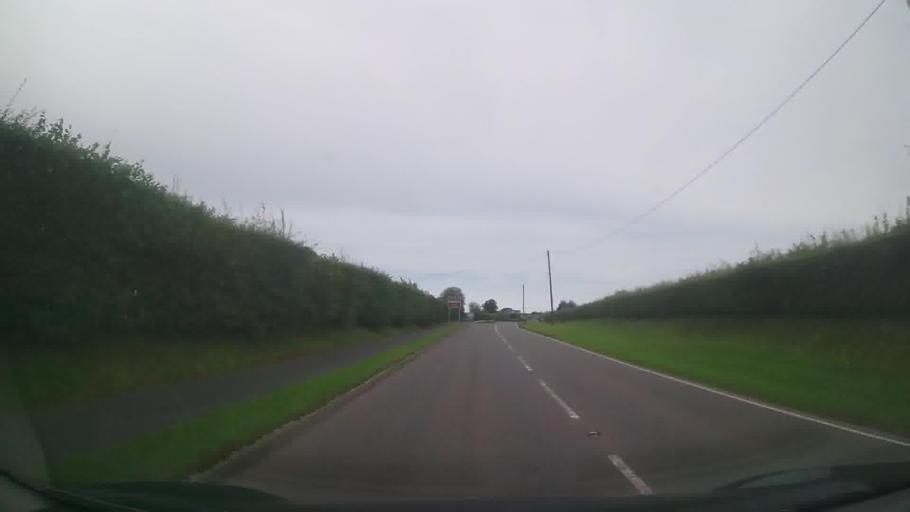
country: GB
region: Wales
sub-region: Pembrokeshire
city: Kilgetty
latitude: 51.7430
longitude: -4.7297
